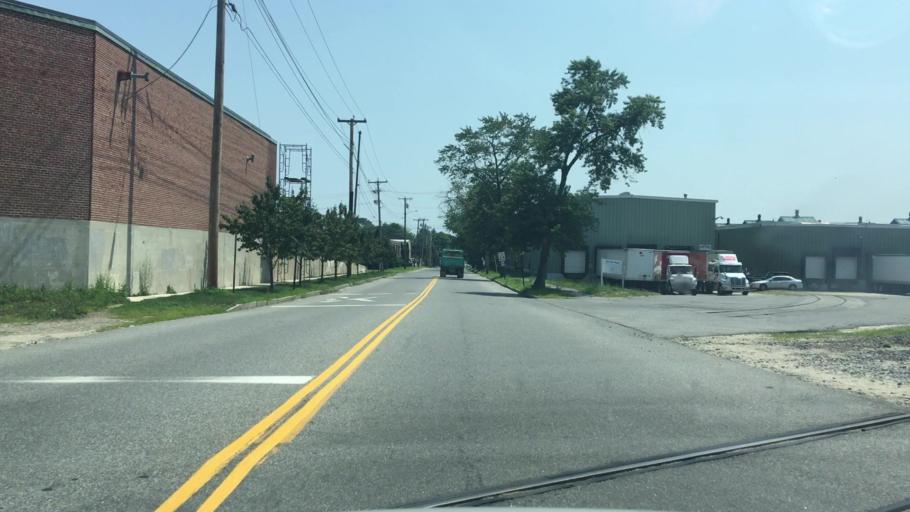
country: US
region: Maine
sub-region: Cumberland County
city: Portland
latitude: 43.6838
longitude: -70.2885
